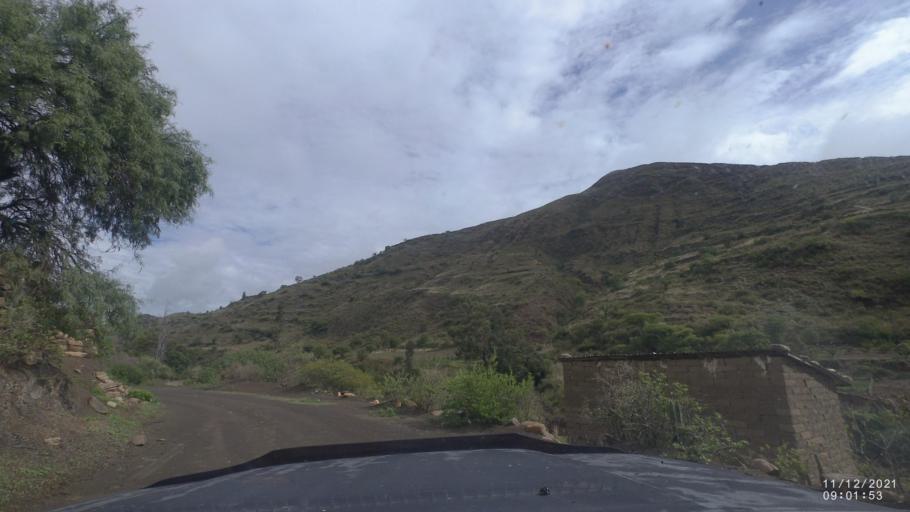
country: BO
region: Cochabamba
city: Tarata
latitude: -17.8988
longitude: -65.9450
